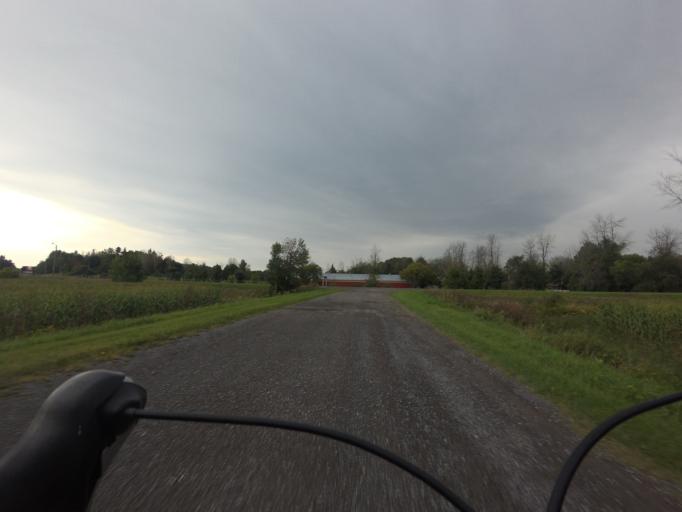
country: CA
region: Ontario
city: Bells Corners
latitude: 45.1579
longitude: -75.7074
